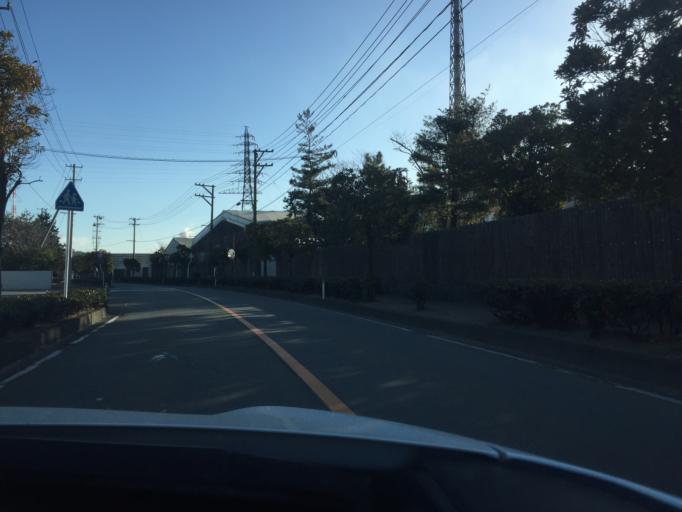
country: JP
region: Fukushima
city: Iwaki
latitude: 36.9390
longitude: 140.8675
